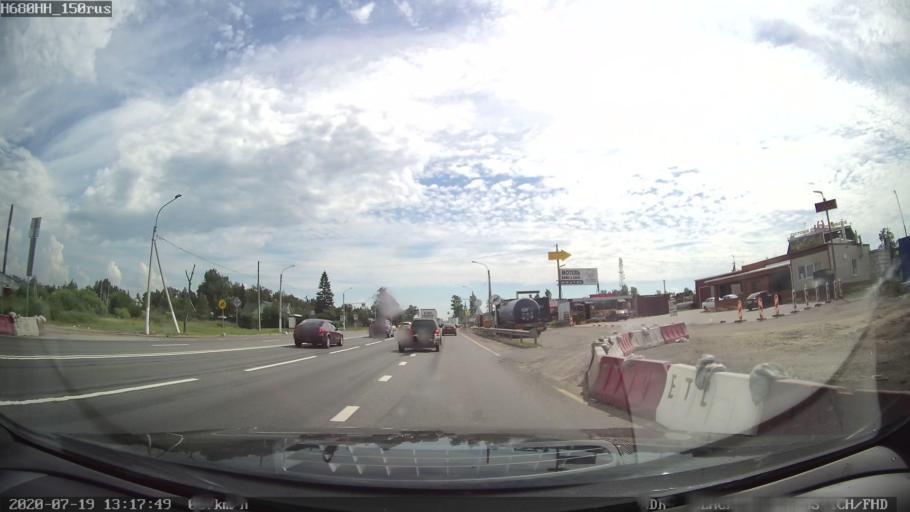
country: RU
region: St.-Petersburg
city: Kolpino
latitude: 59.7057
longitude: 30.5756
